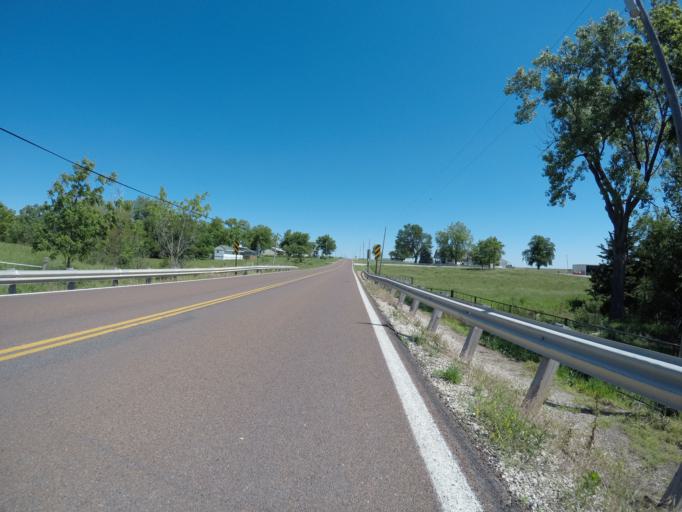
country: US
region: Kansas
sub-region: Wabaunsee County
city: Alma
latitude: 38.8663
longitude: -96.1041
